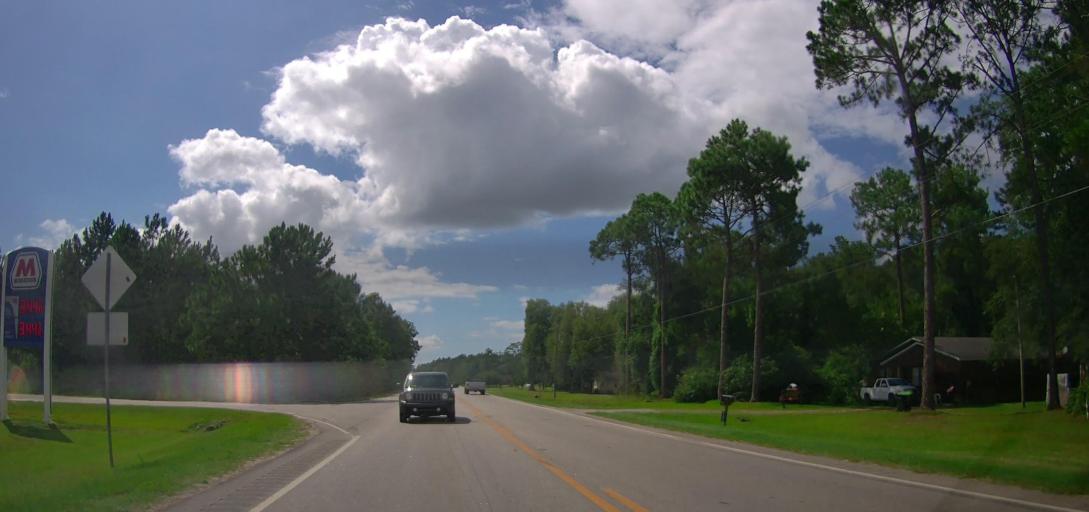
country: US
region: Georgia
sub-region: Coffee County
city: Broxton
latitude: 31.5560
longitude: -82.9669
